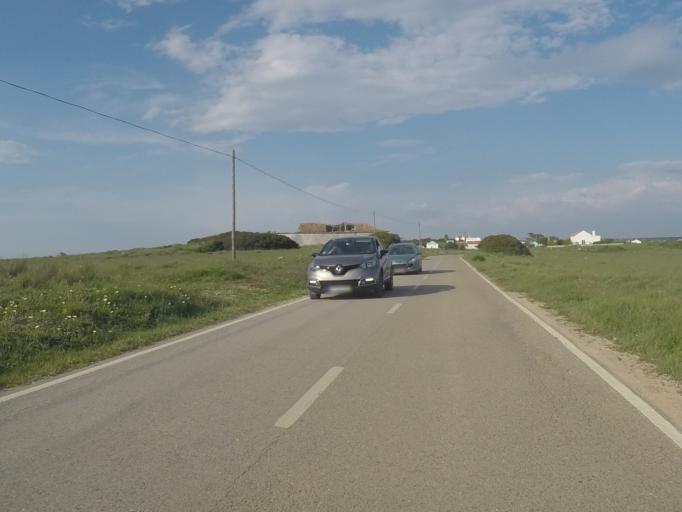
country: PT
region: Setubal
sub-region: Sesimbra
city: Sesimbra
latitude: 38.4244
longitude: -9.1959
